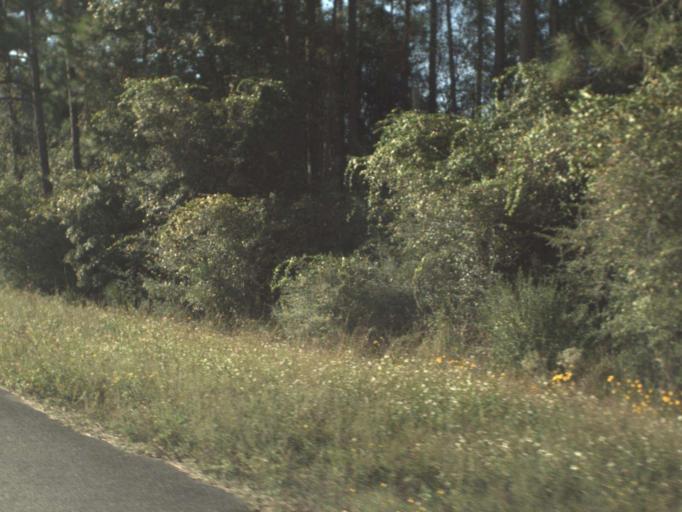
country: US
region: Florida
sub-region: Bay County
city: Laguna Beach
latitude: 30.4410
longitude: -85.8641
